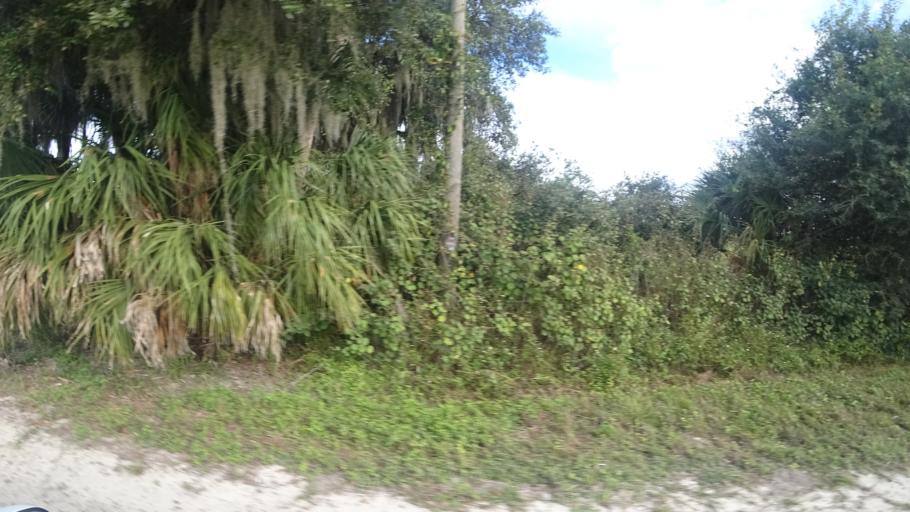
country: US
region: Florida
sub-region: Sarasota County
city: Warm Mineral Springs
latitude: 27.2435
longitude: -82.1670
